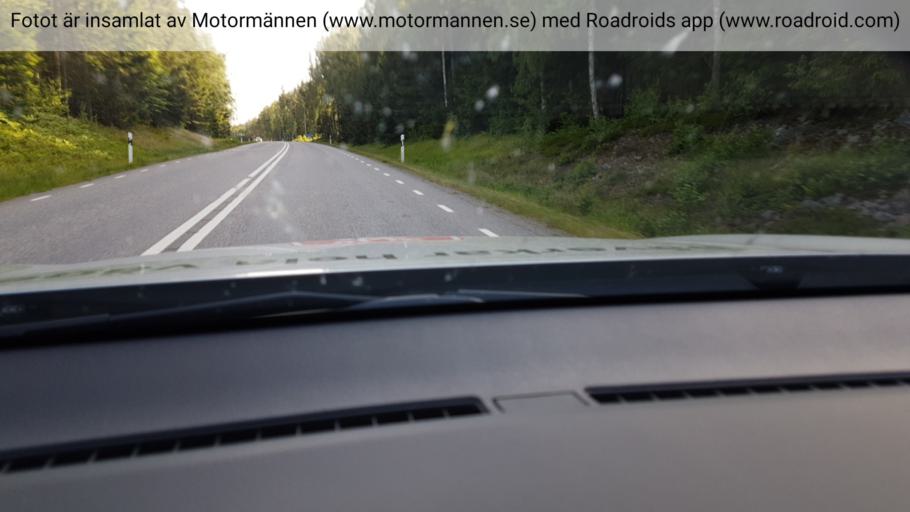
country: SE
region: Joenkoeping
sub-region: Varnamo Kommun
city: Bor
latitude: 57.2565
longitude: 14.1849
